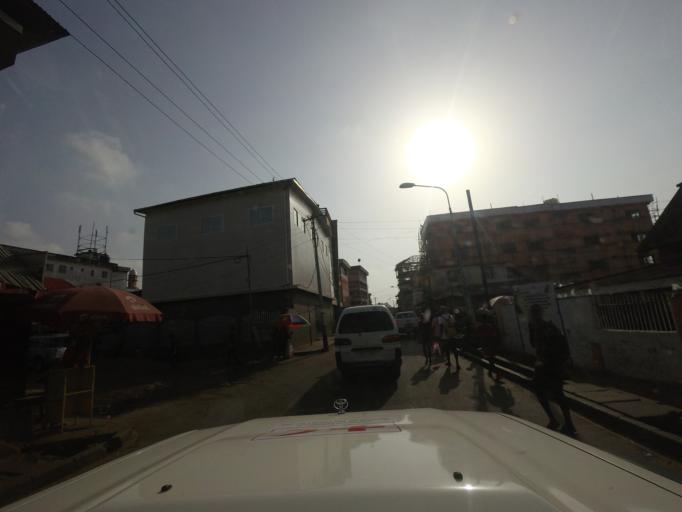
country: SL
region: Western Area
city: Freetown
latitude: 8.4835
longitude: -13.2413
